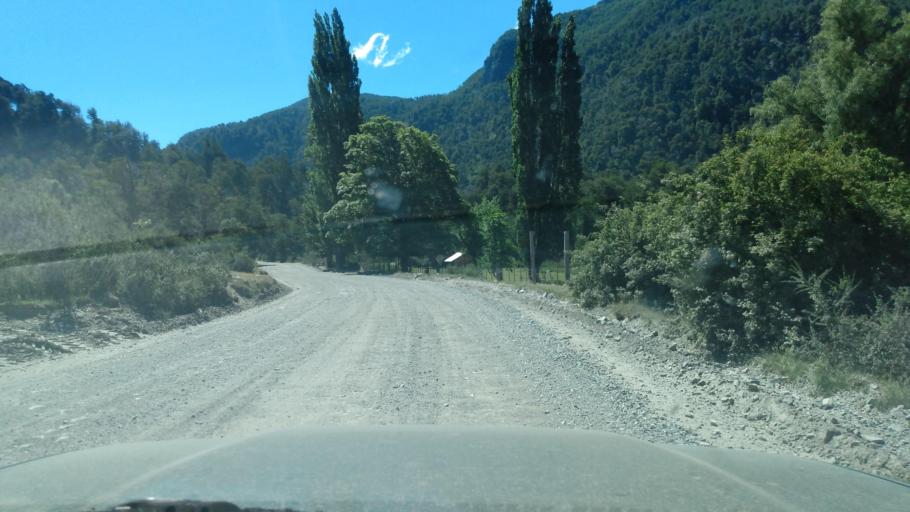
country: AR
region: Neuquen
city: Villa La Angostura
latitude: -40.6091
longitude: -71.6126
